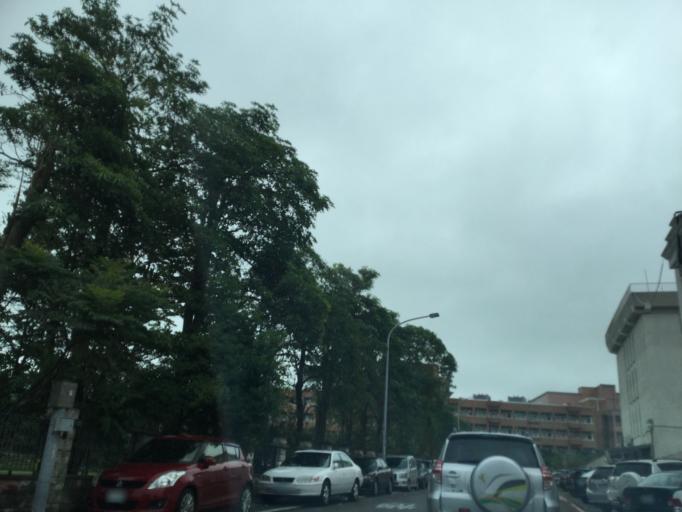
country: TW
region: Taiwan
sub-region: Hsinchu
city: Hsinchu
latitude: 24.7992
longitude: 121.0004
